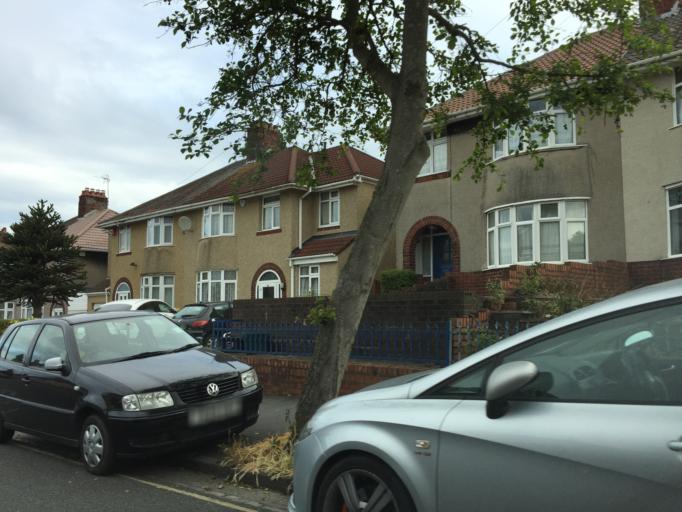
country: GB
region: England
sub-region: Bristol
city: Bristol
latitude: 51.4982
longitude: -2.5866
